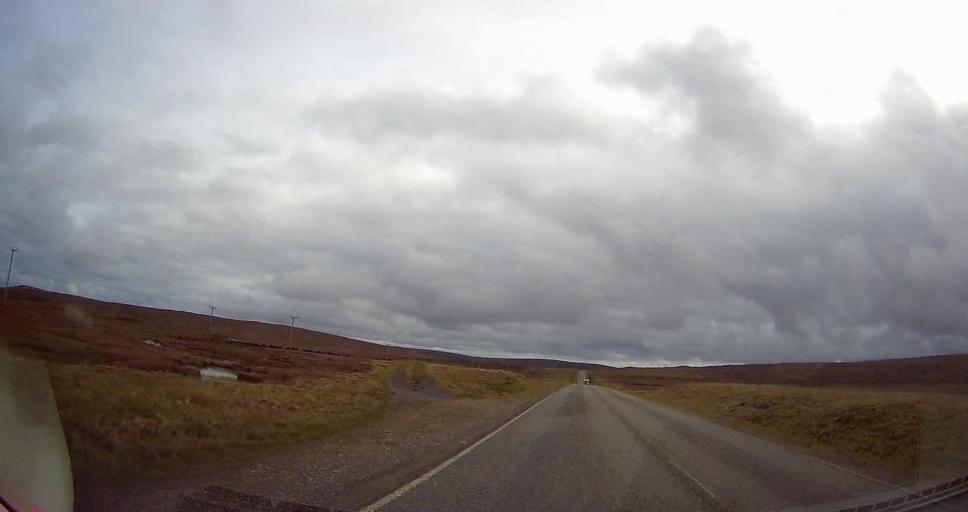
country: GB
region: Scotland
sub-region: Shetland Islands
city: Shetland
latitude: 60.5955
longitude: -1.1486
